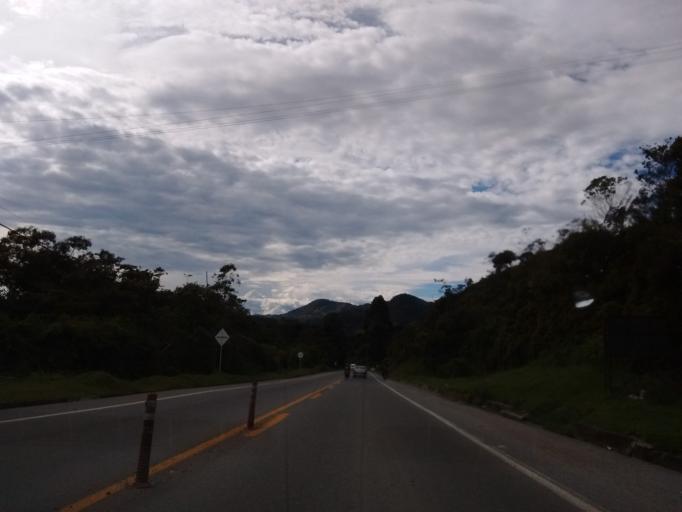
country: CO
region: Antioquia
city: Santuario
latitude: 6.1143
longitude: -75.2312
